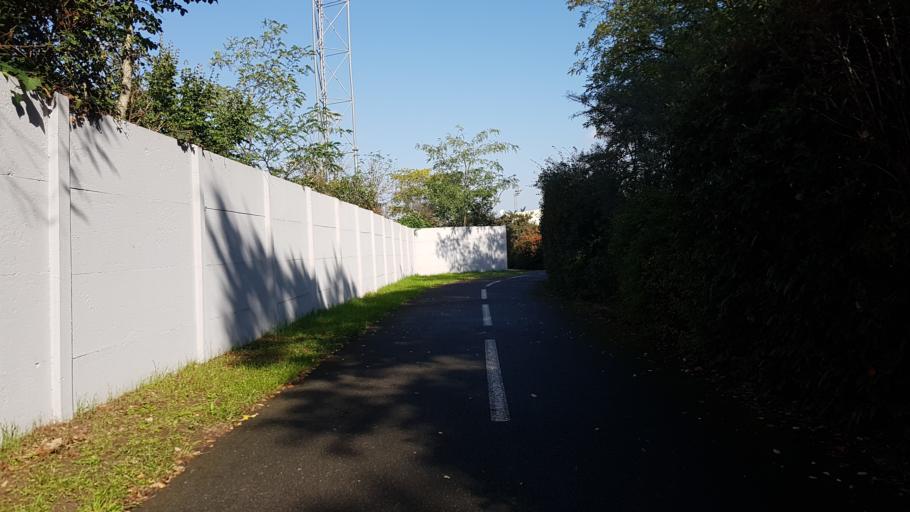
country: FR
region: Poitou-Charentes
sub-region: Departement de la Vienne
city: Chasseneuil-du-Poitou
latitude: 46.6549
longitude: 0.3755
